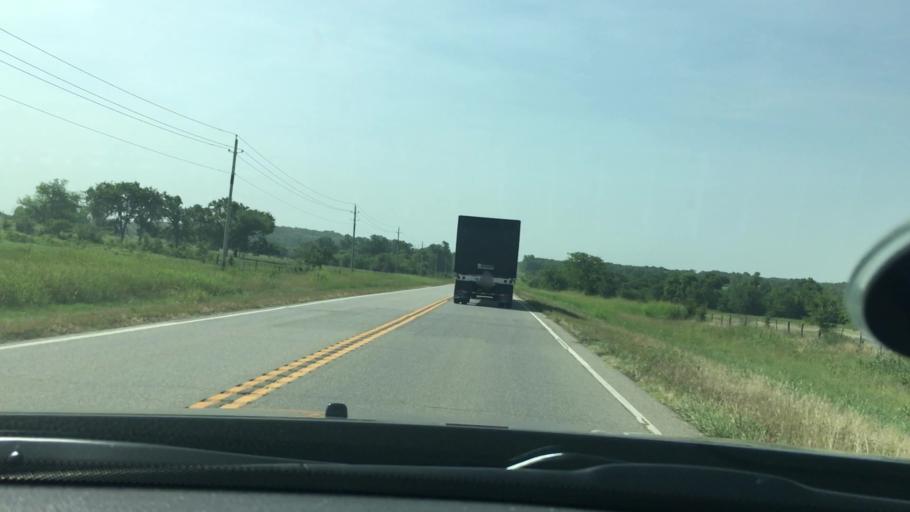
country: US
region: Oklahoma
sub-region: Coal County
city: Coalgate
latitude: 34.4562
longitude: -96.2130
